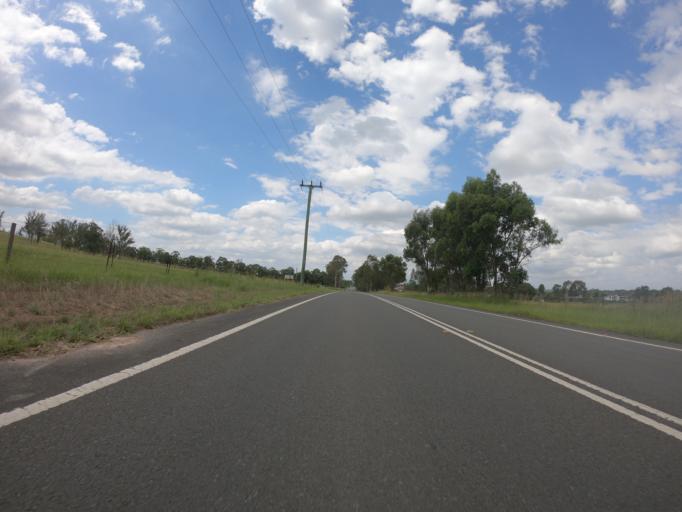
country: AU
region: New South Wales
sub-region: Liverpool
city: Luddenham
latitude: -33.8384
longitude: 150.7475
